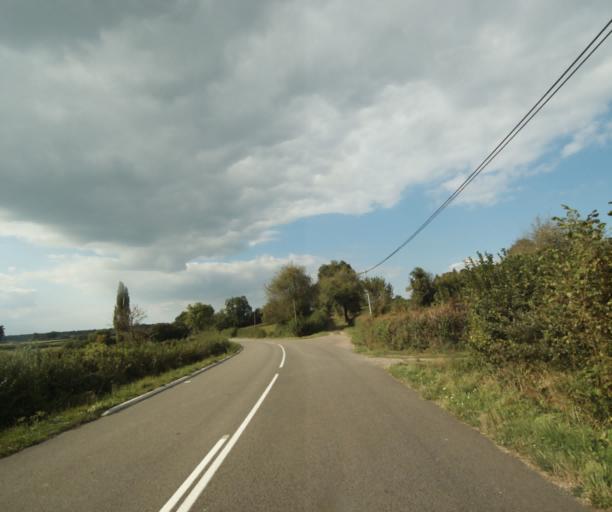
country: FR
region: Bourgogne
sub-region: Departement de Saone-et-Loire
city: Palinges
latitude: 46.5119
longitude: 4.2588
